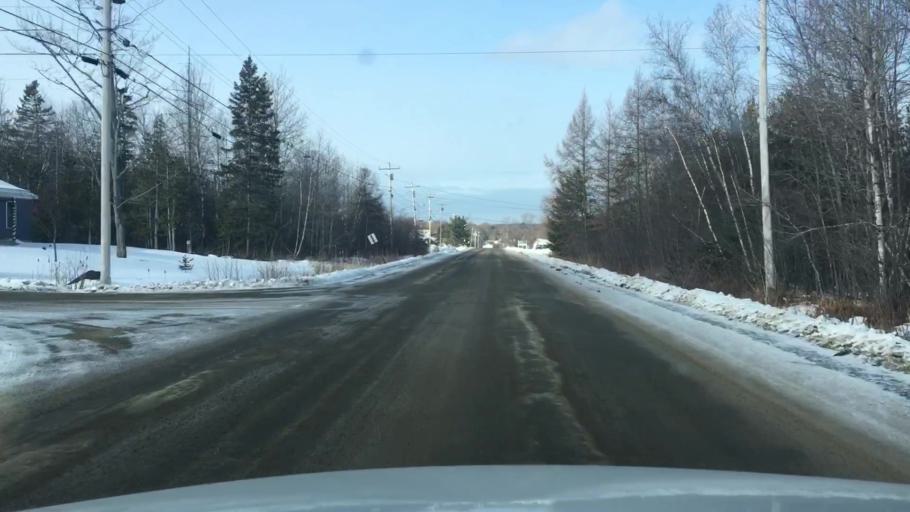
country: US
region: Maine
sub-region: Washington County
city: Calais
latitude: 45.1787
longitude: -67.2650
